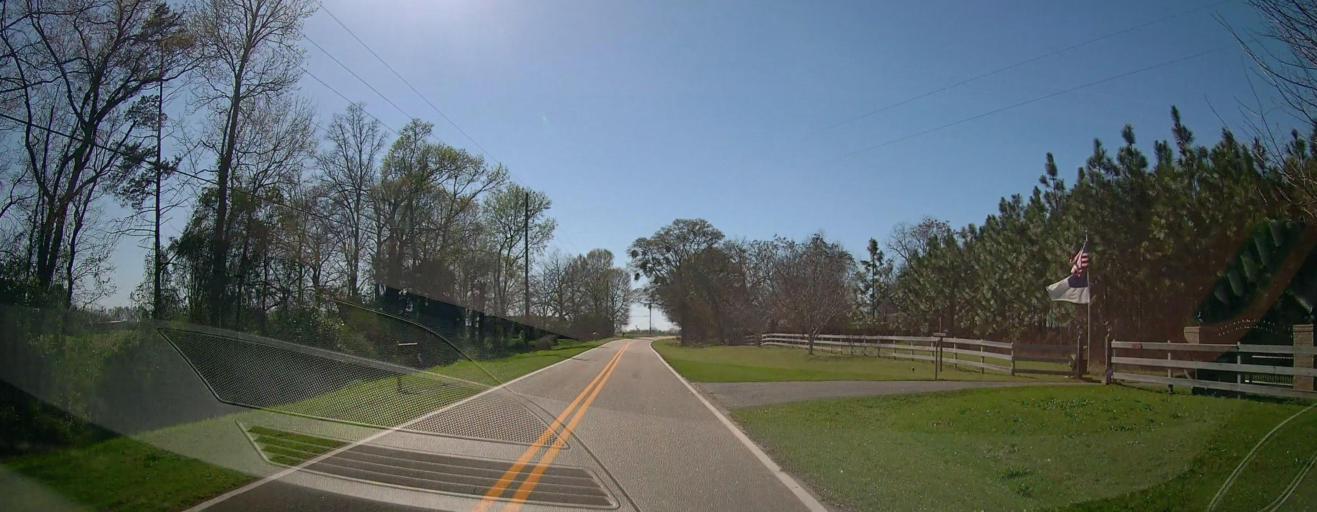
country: US
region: Georgia
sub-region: Peach County
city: Fort Valley
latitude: 32.6120
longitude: -83.9080
